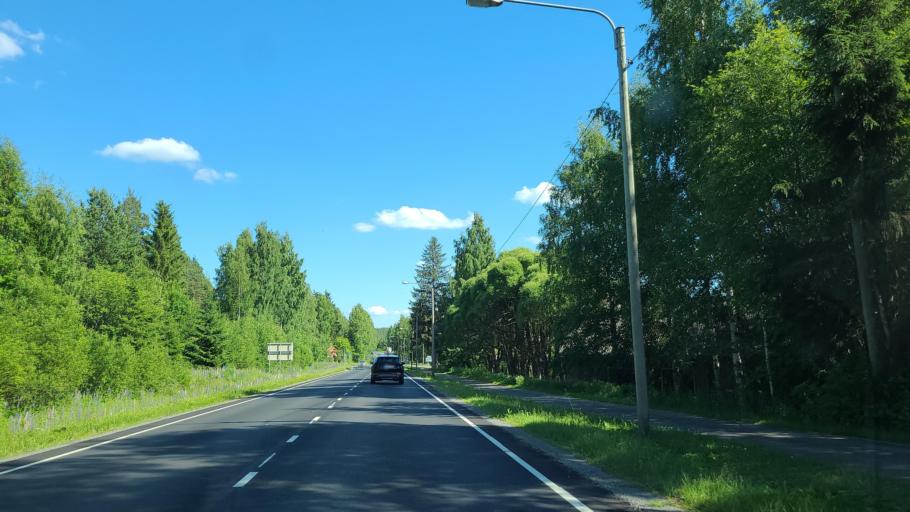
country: FI
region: Central Finland
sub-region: Jyvaeskylae
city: Petaejaevesi
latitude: 62.2601
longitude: 25.1896
